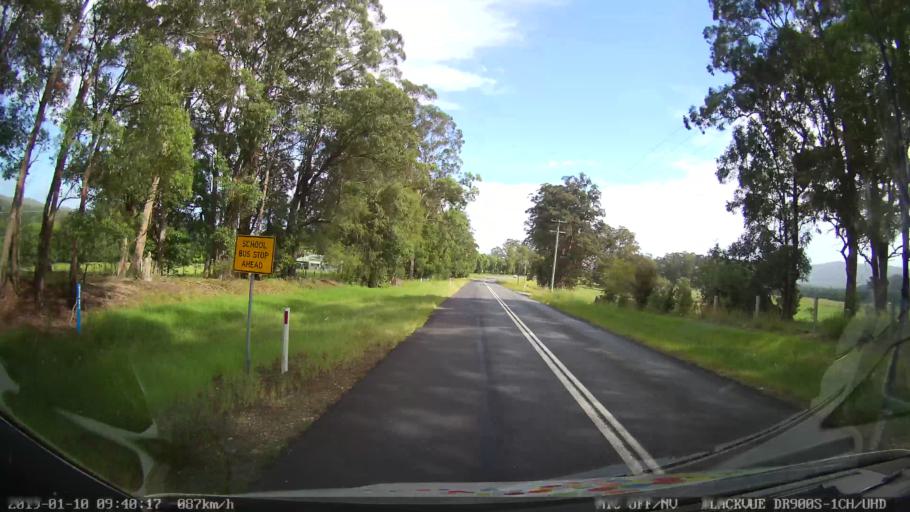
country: AU
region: New South Wales
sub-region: Coffs Harbour
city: Nana Glen
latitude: -30.1536
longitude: 153.0054
